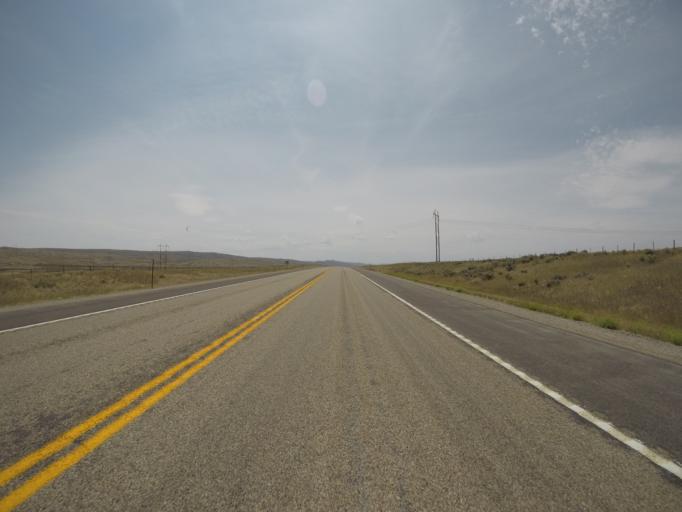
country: US
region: Wyoming
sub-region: Lincoln County
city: Kemmerer
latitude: 41.7454
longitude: -110.5643
